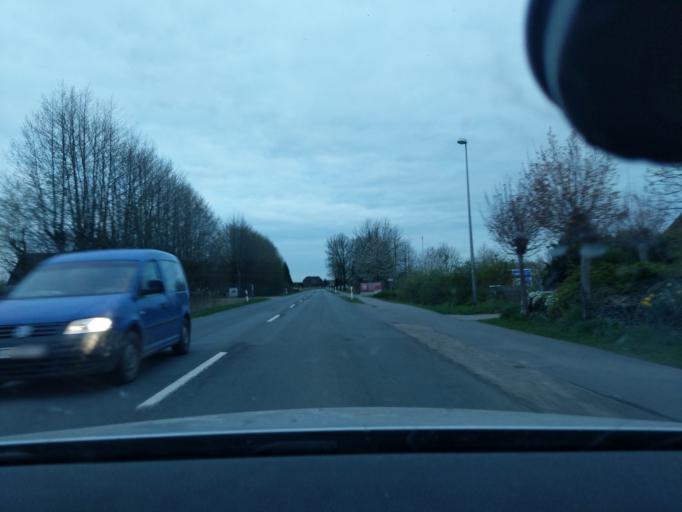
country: DE
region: Lower Saxony
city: Jork
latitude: 53.5220
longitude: 9.7367
